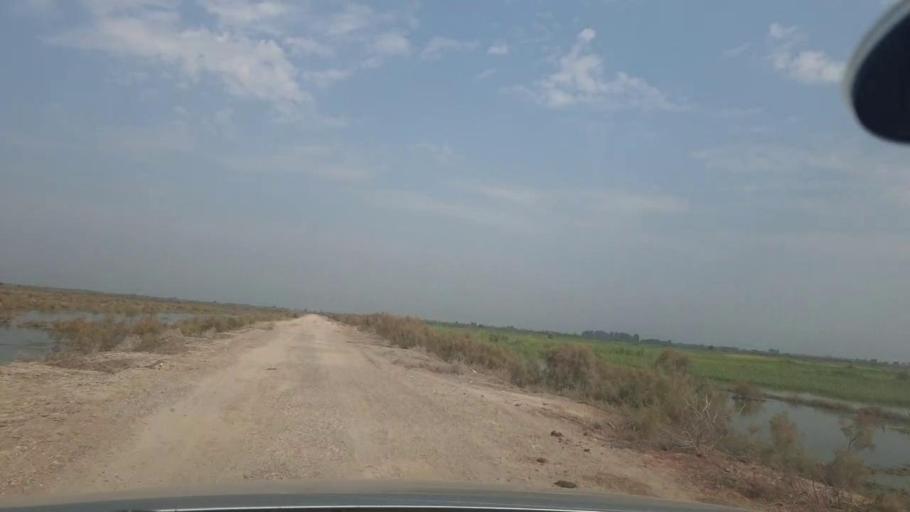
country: PK
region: Balochistan
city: Mehrabpur
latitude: 28.0388
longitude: 68.1252
